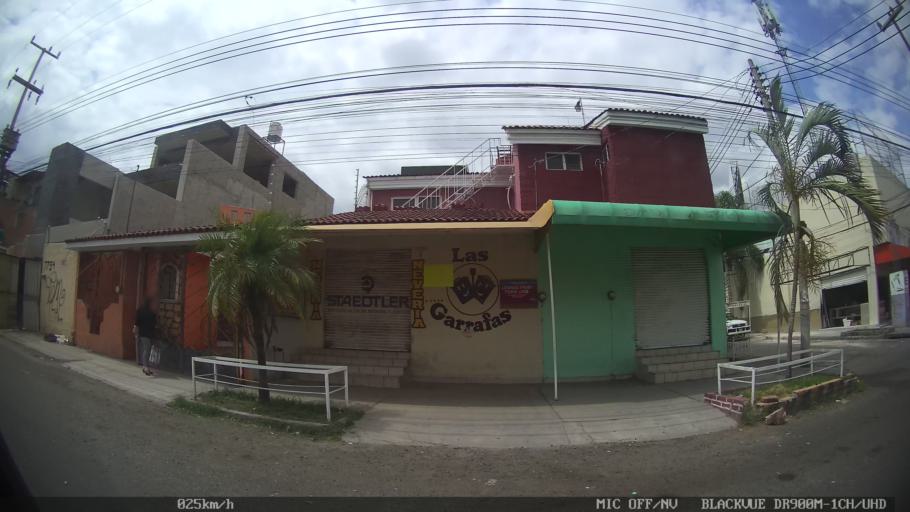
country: MX
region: Jalisco
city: Tlaquepaque
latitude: 20.6313
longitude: -103.2660
